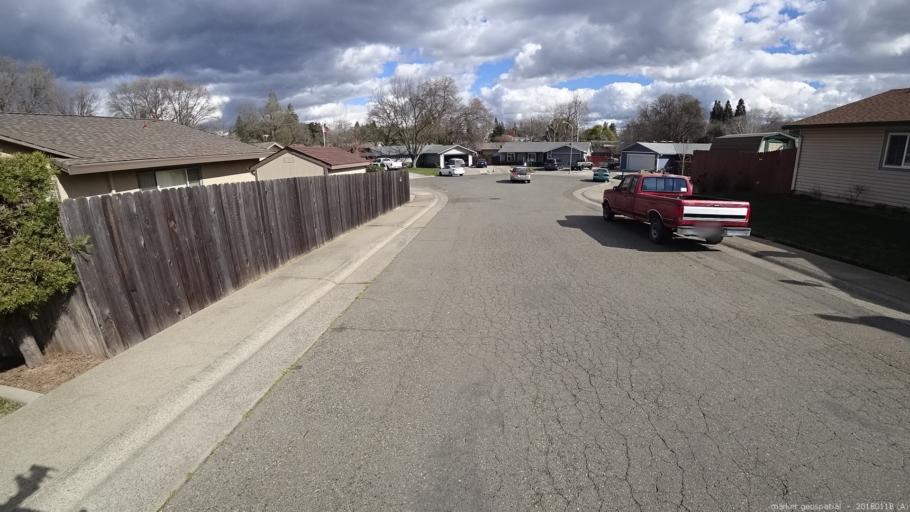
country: US
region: California
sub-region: Sacramento County
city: Orangevale
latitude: 38.6733
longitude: -121.2133
